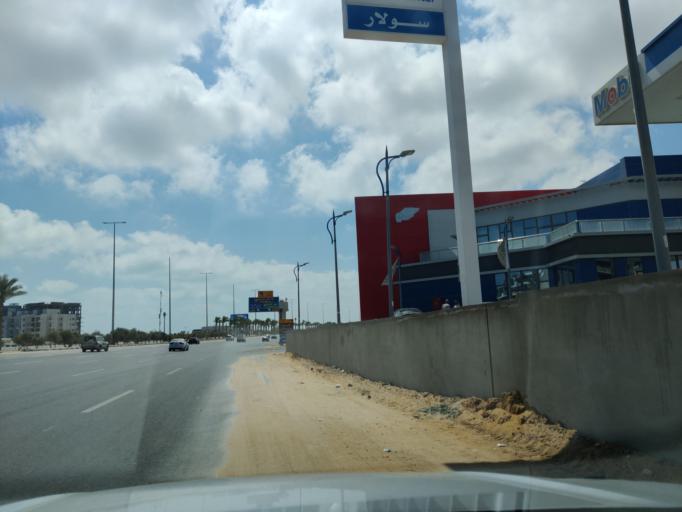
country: EG
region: Muhafazat Matruh
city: Al `Alamayn
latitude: 30.8450
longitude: 28.9406
